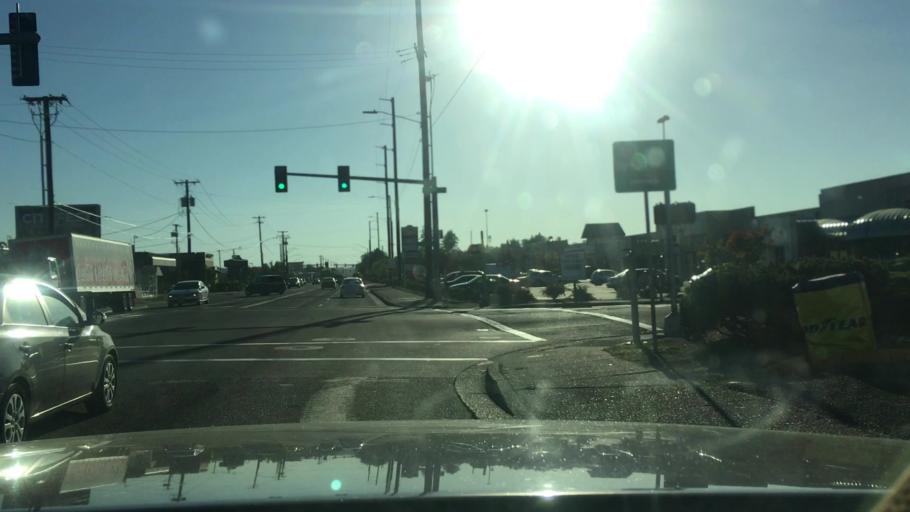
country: US
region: Oregon
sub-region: Lane County
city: Eugene
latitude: 44.0480
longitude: -123.1365
